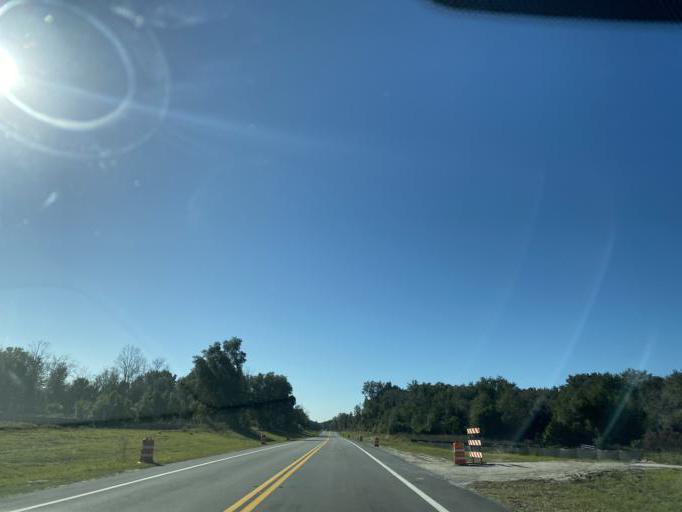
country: US
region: Florida
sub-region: Lake County
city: Mount Plymouth
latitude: 28.8236
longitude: -81.5218
